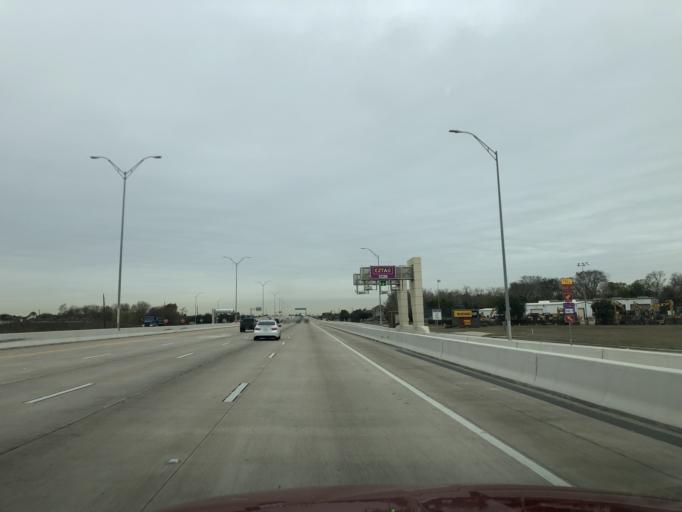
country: US
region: Texas
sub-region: Fort Bend County
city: Missouri City
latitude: 29.6327
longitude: -95.5253
